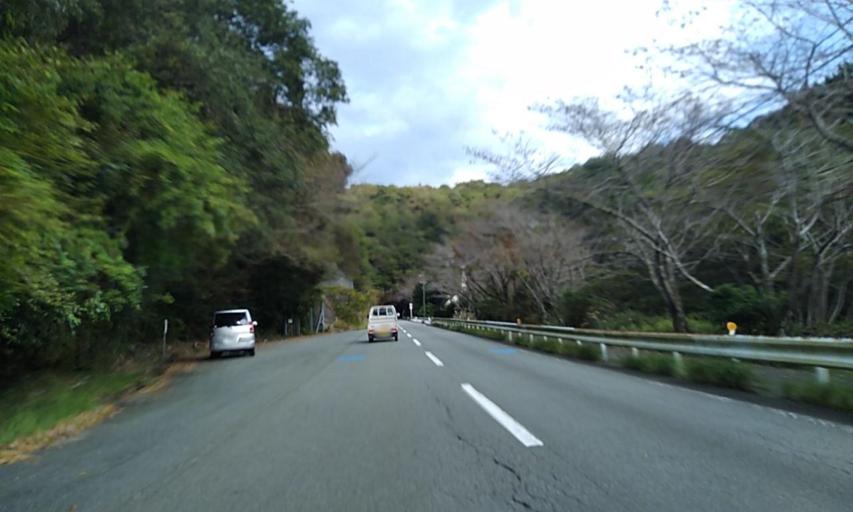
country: JP
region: Mie
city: Ise
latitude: 34.2956
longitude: 136.5842
